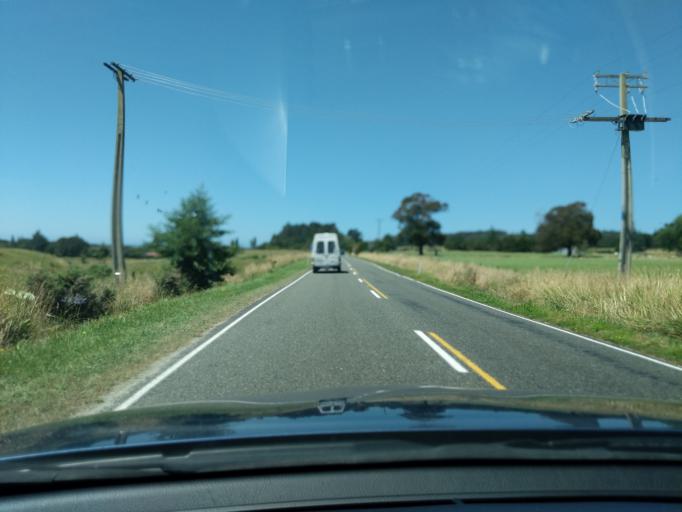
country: NZ
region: Tasman
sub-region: Tasman District
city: Takaka
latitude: -40.6847
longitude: 172.6579
